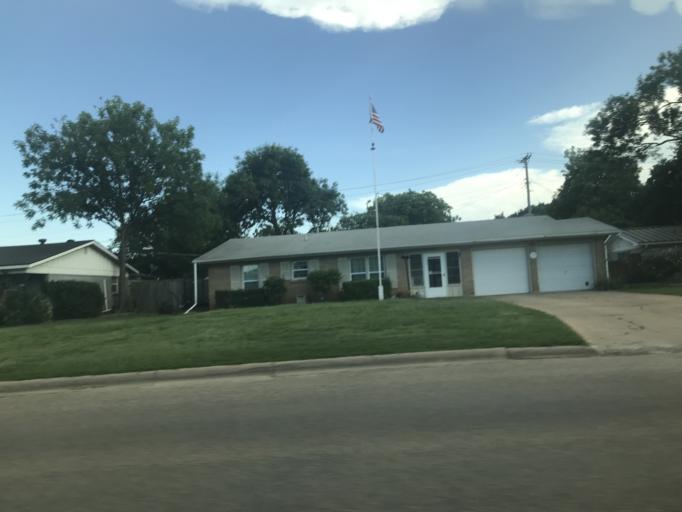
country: US
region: Texas
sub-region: Taylor County
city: Abilene
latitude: 32.4245
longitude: -99.7675
